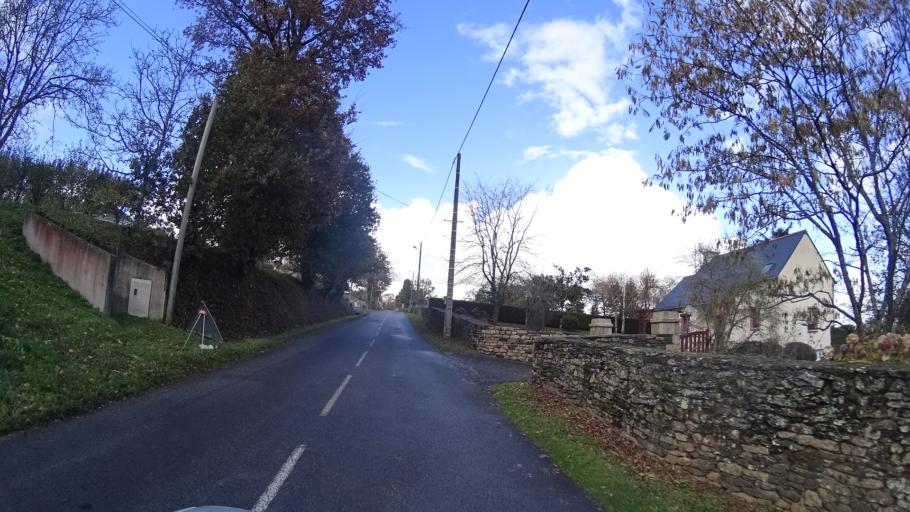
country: FR
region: Brittany
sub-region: Departement du Morbihan
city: Saint-Jean-la-Poterie
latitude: 47.6465
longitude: -2.1204
